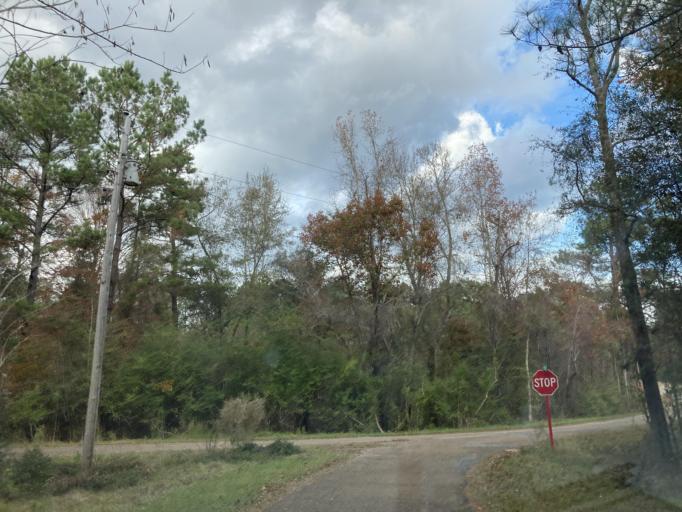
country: US
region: Mississippi
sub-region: Lamar County
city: Purvis
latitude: 31.1627
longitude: -89.6209
